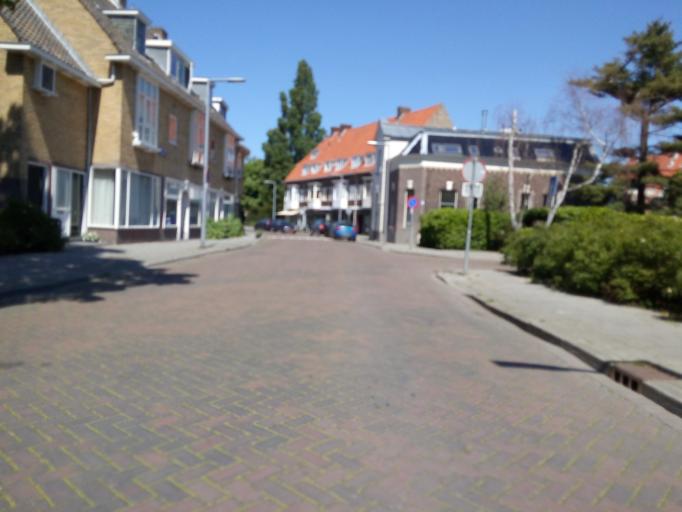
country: NL
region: South Holland
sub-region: Gemeente Schiedam
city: Schiedam
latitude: 51.9376
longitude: 4.4221
